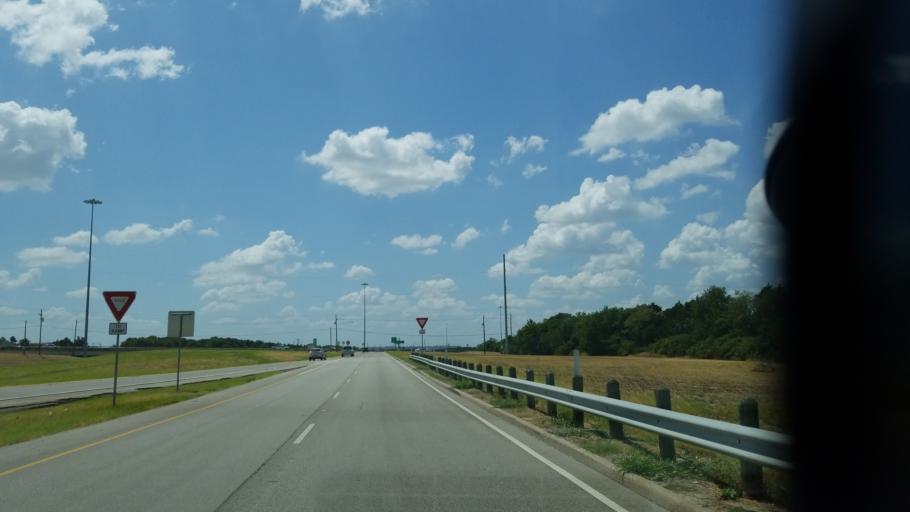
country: US
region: Texas
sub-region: Dallas County
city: Cockrell Hill
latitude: 32.7227
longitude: -96.9194
